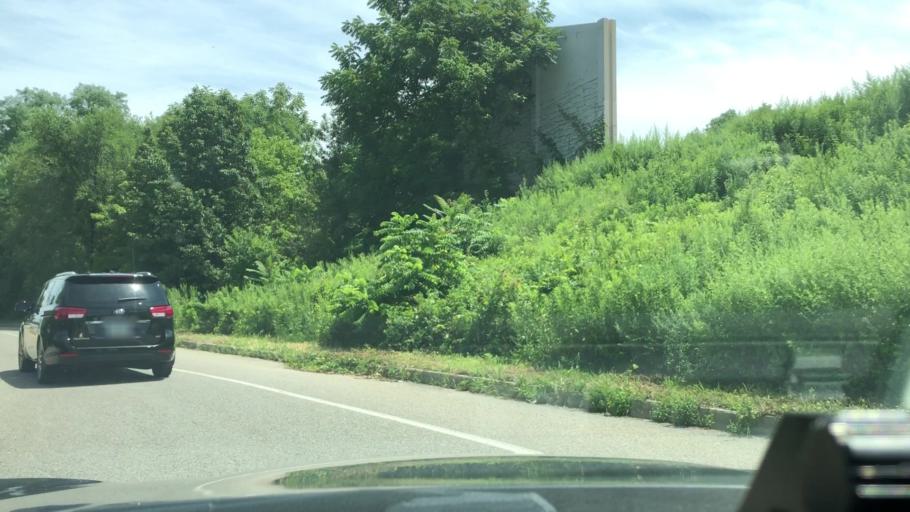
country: US
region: Pennsylvania
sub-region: Chester County
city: Devon
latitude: 40.0734
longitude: -75.4302
